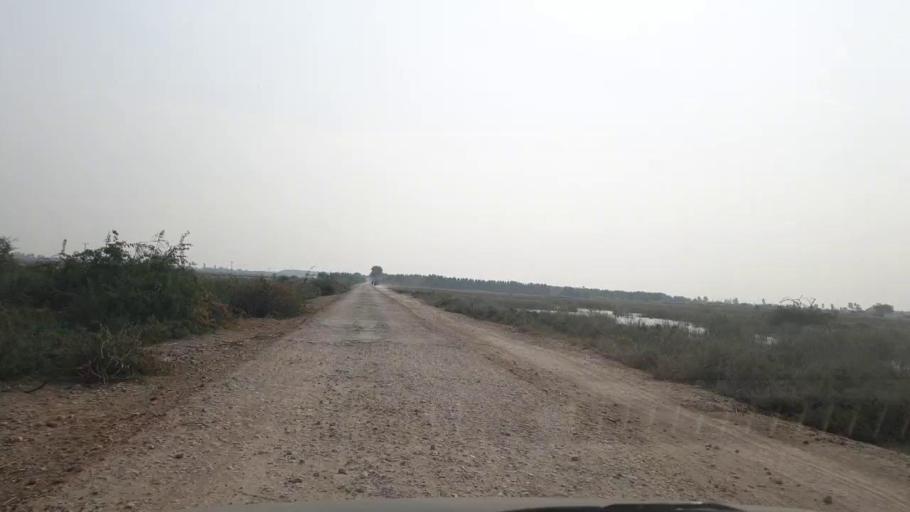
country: PK
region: Sindh
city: Tando Muhammad Khan
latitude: 25.0465
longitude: 68.3897
